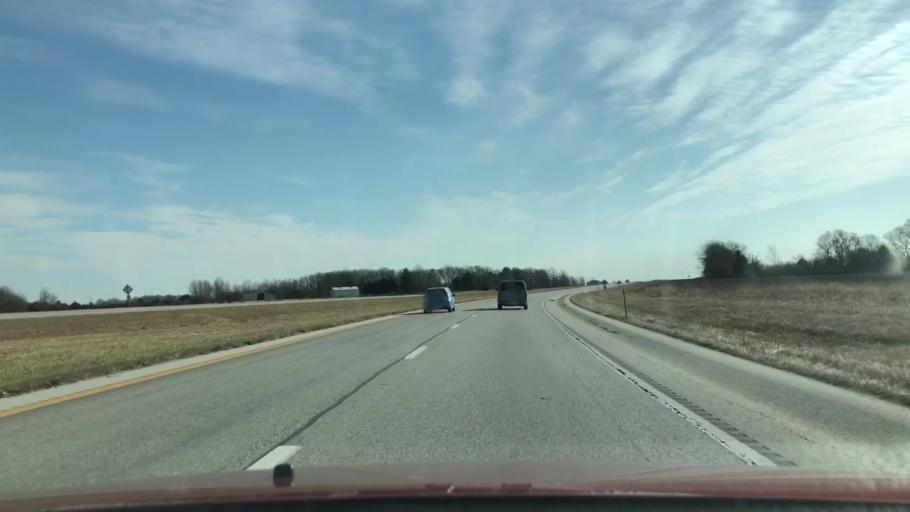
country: US
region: Missouri
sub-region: Webster County
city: Seymour
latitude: 37.1679
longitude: -92.8065
